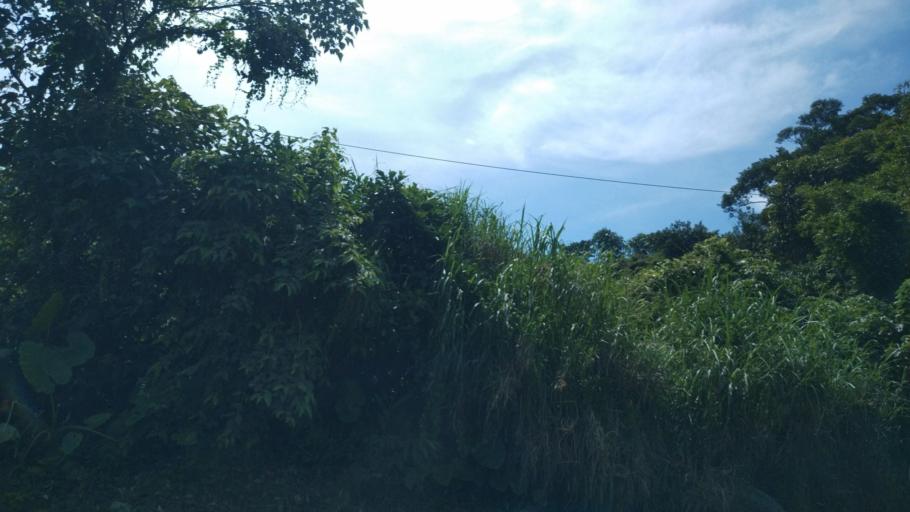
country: TW
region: Taipei
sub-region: Taipei
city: Banqiao
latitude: 24.9497
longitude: 121.5053
